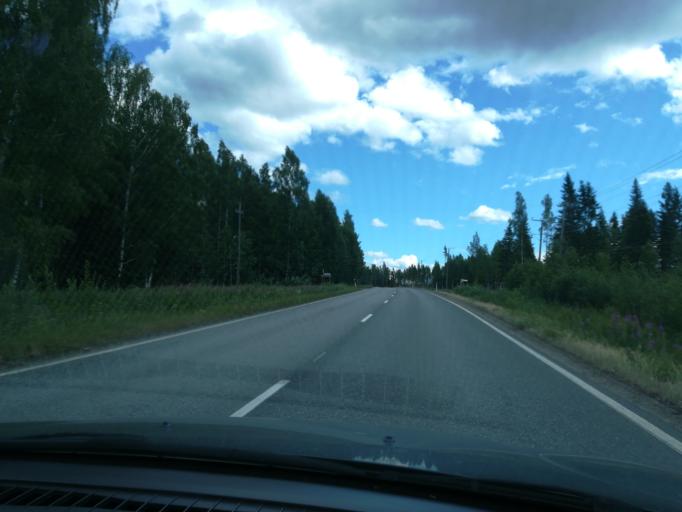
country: FI
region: Southern Savonia
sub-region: Mikkeli
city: Hirvensalmi
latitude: 61.6691
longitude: 26.8057
